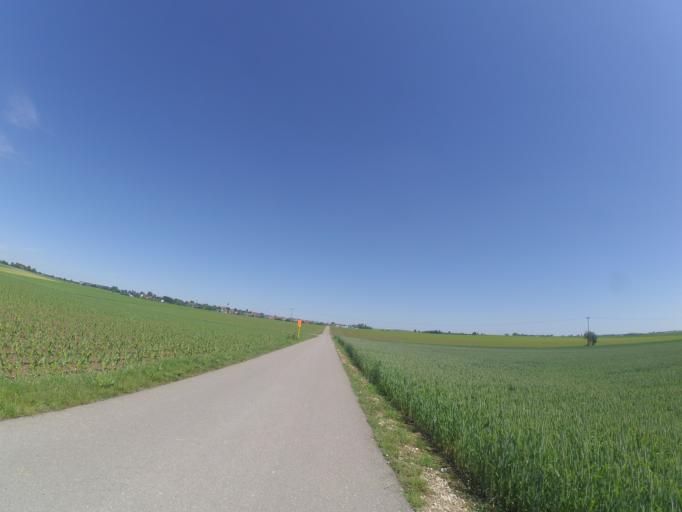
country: DE
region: Baden-Wuerttemberg
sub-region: Tuebingen Region
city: Dornstadt
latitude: 48.4719
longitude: 9.9163
